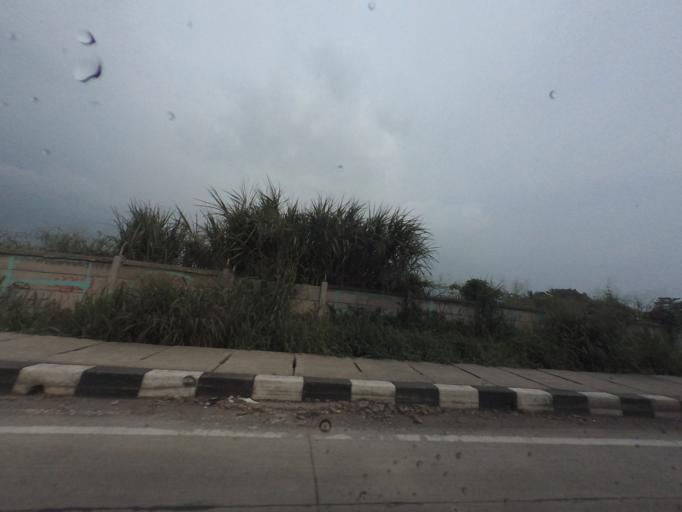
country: ID
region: West Java
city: Cicurug
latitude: -6.7531
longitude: 106.7996
